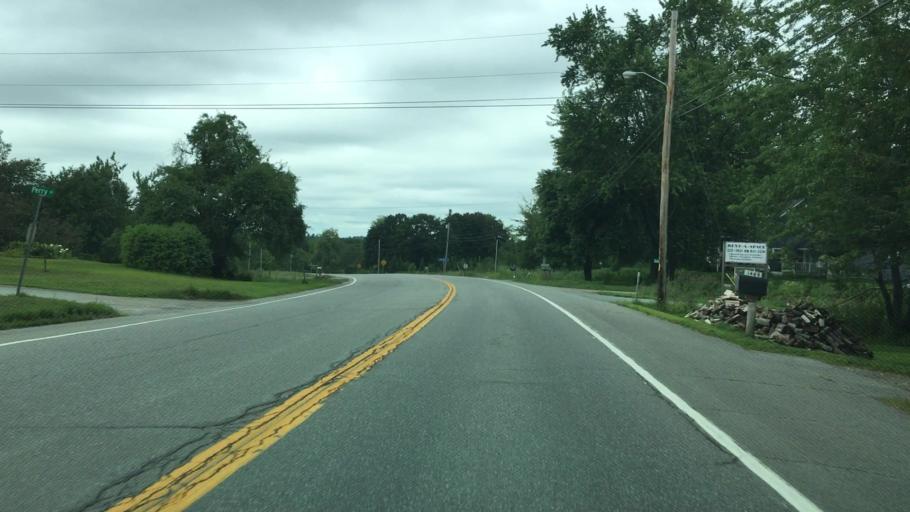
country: US
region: Maine
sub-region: Penobscot County
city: Orrington
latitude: 44.6866
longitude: -68.8458
